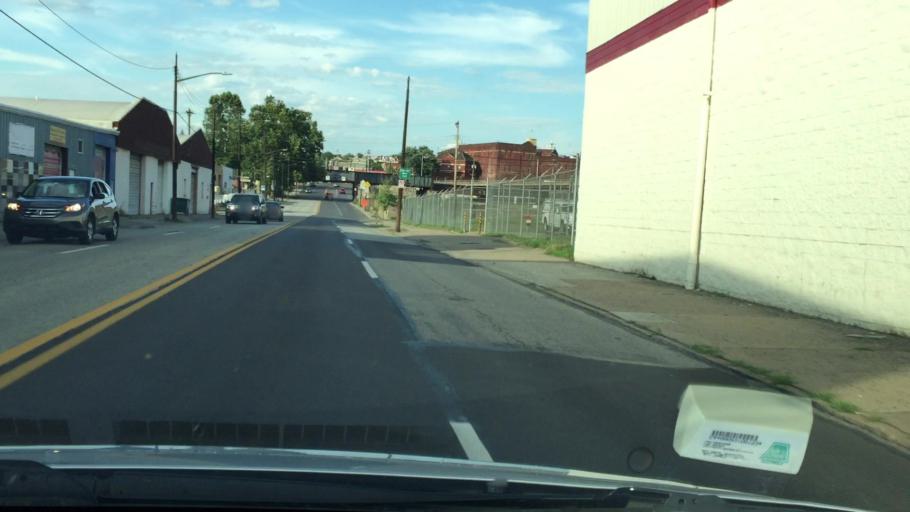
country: US
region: Pennsylvania
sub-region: Allegheny County
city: Bloomfield
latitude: 40.4596
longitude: -79.9701
